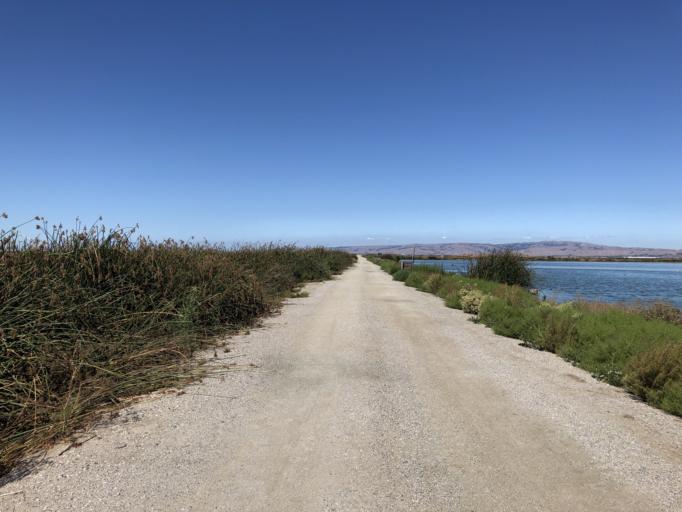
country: US
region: California
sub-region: Santa Clara County
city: Sunnyvale
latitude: 37.4284
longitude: -122.0171
